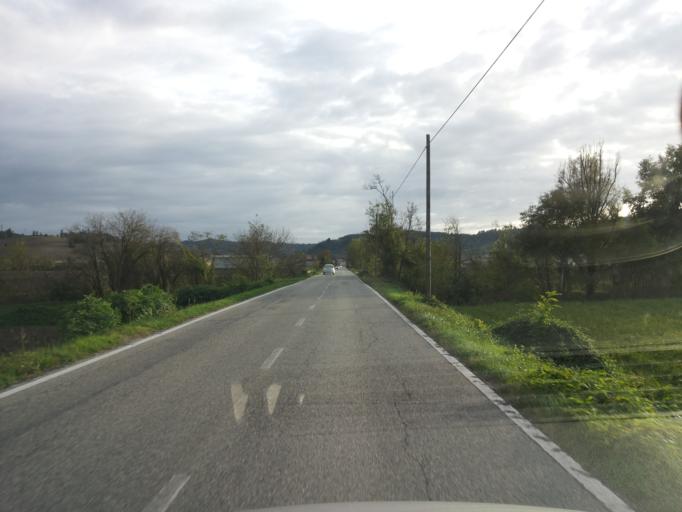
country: IT
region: Piedmont
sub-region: Provincia di Alessandria
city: Cereseto
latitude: 45.1101
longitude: 8.3090
